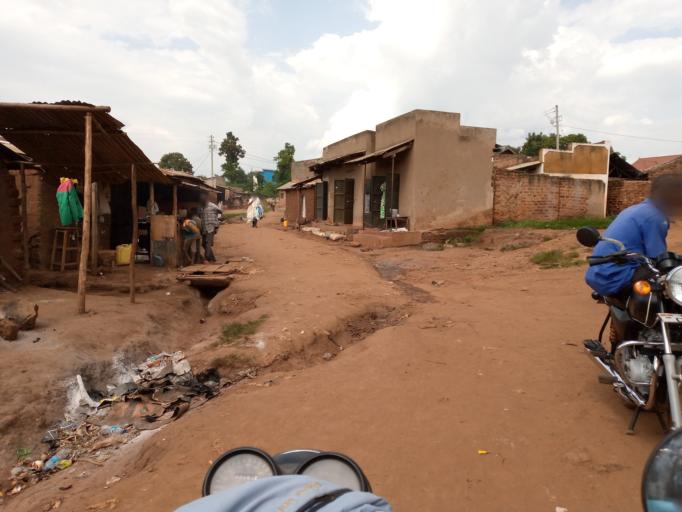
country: UG
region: Eastern Region
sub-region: Mbale District
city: Mbale
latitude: 1.0824
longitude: 34.1650
